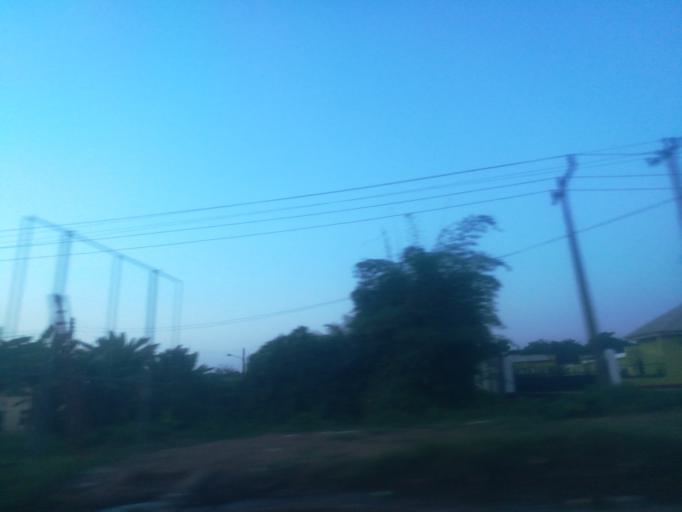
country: NG
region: Ogun
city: Abeokuta
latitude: 7.1860
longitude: 3.4317
